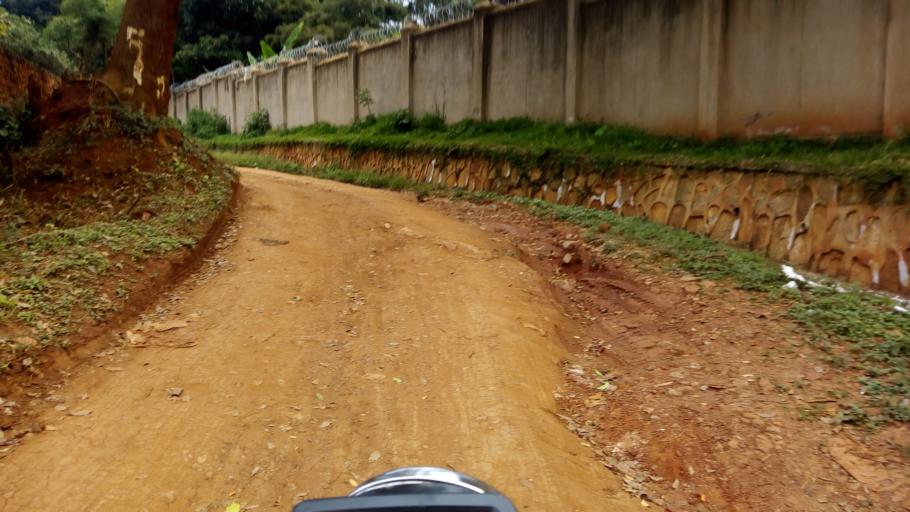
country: UG
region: Central Region
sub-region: Wakiso District
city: Kireka
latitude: 0.3282
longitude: 32.6345
